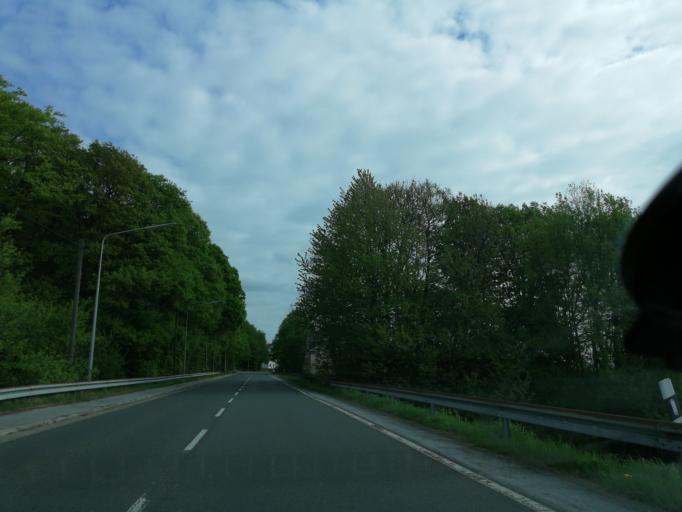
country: DE
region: North Rhine-Westphalia
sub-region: Regierungsbezirk Arnsberg
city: Schwelm
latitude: 51.3137
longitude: 7.2907
